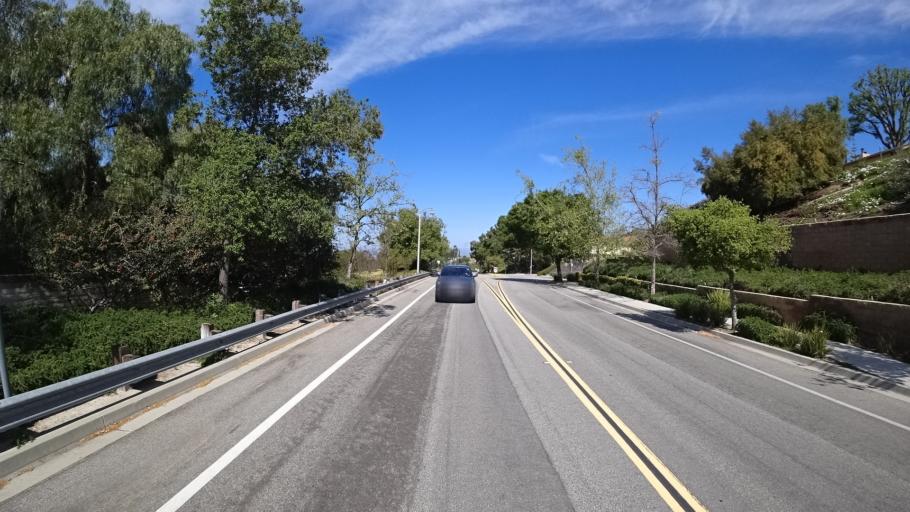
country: US
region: California
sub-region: Ventura County
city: Thousand Oaks
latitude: 34.2241
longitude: -118.8378
